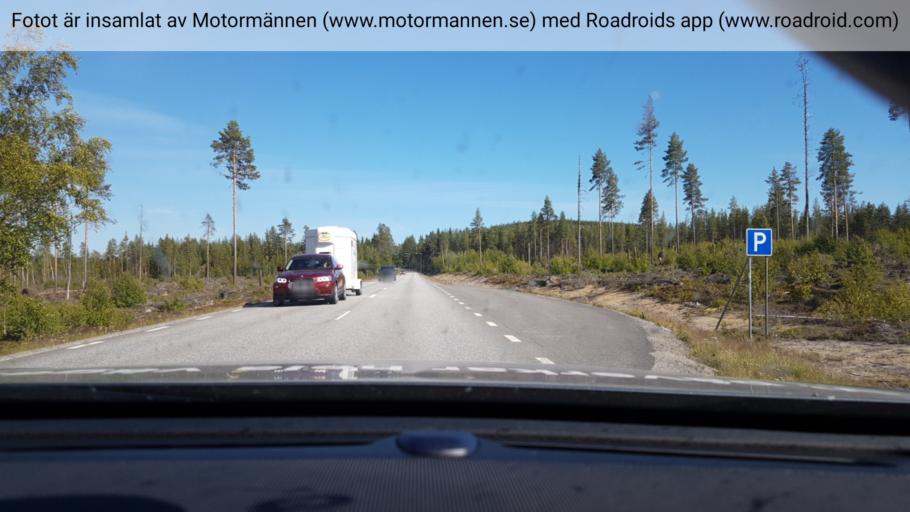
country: SE
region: Vaesterbotten
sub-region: Lycksele Kommun
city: Lycksele
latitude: 64.6441
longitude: 18.5067
